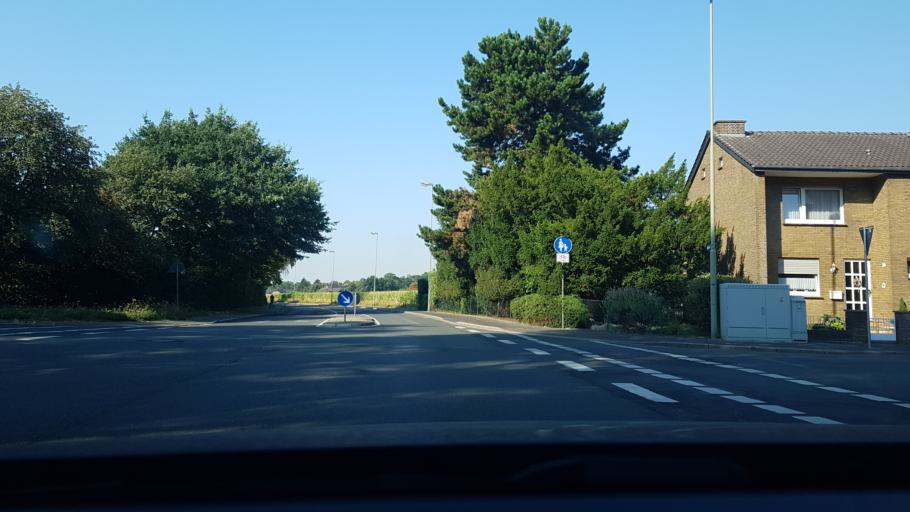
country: DE
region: North Rhine-Westphalia
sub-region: Regierungsbezirk Dusseldorf
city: Kamp-Lintfort
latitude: 51.4555
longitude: 6.5748
